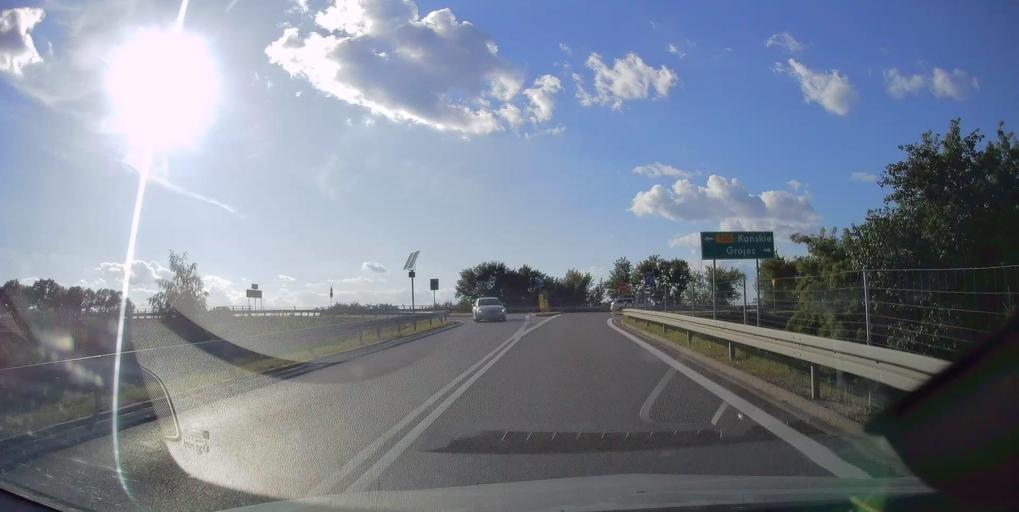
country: PL
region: Masovian Voivodeship
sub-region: Powiat grojecki
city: Grojec
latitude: 51.8608
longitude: 20.8564
